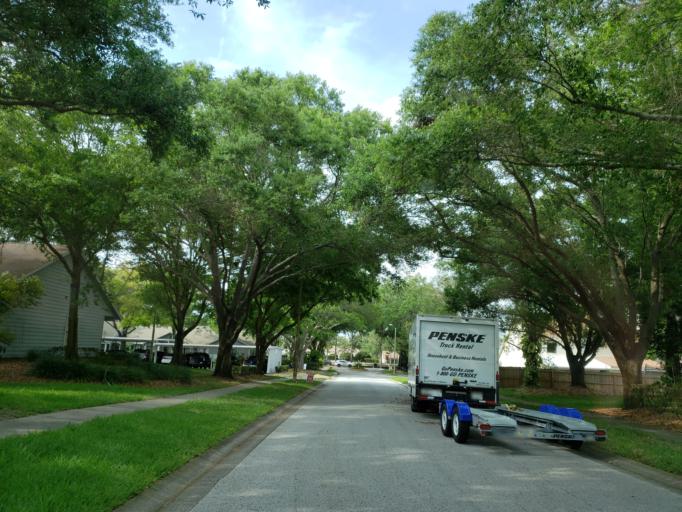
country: US
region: Florida
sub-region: Pinellas County
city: Saint George
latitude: 28.0923
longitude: -82.7306
